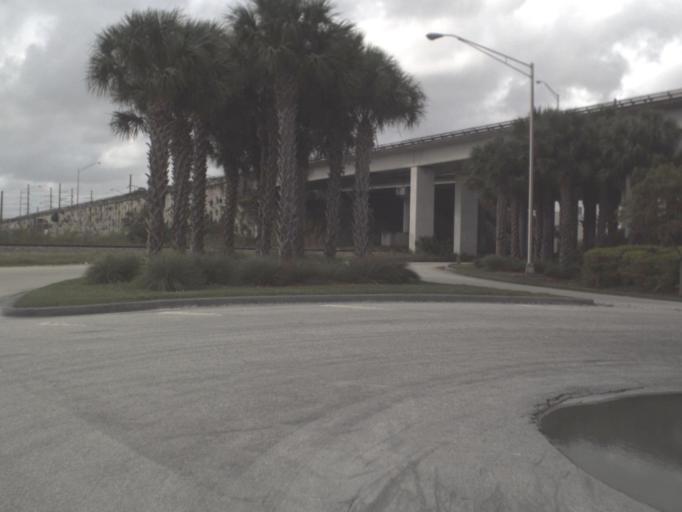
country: US
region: Florida
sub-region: Miami-Dade County
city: Miami Springs
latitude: 25.8393
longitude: -80.3092
